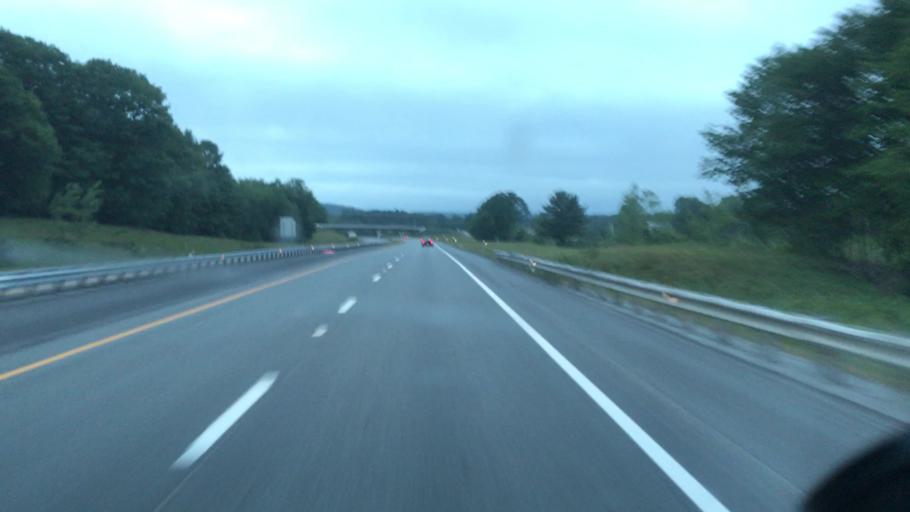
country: US
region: Maine
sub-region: Androscoggin County
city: Lewiston
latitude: 44.0671
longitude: -70.1609
